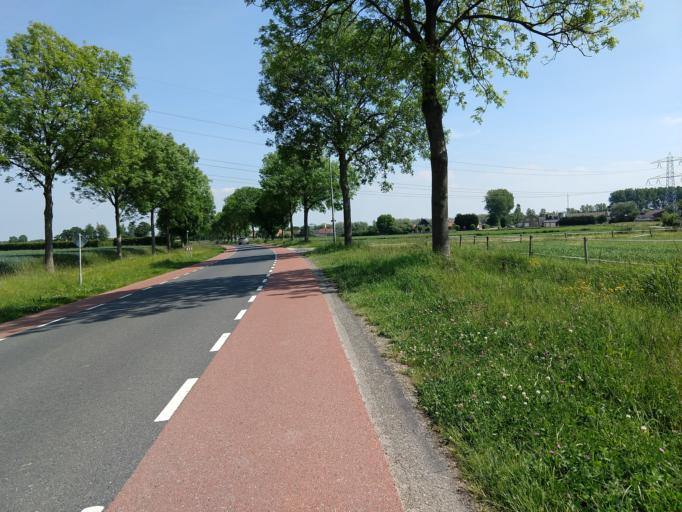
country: NL
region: Zeeland
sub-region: Gemeente Borsele
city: Borssele
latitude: 51.4342
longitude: 3.8094
